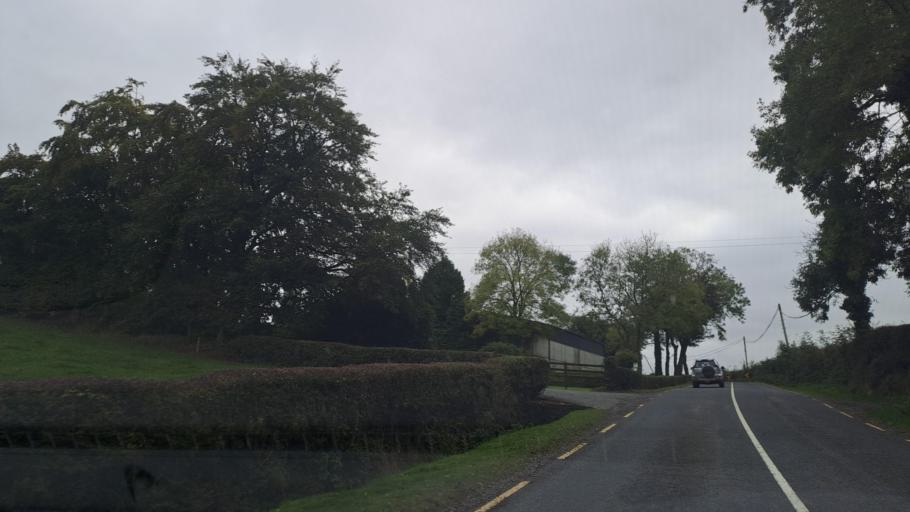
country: IE
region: Ulster
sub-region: An Cabhan
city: Cootehill
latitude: 54.0474
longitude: -7.0498
